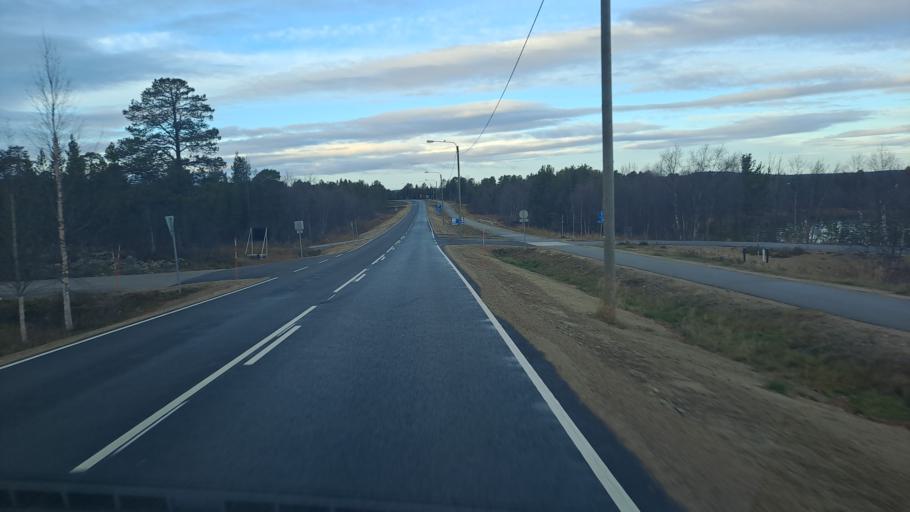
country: FI
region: Lapland
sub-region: Pohjois-Lappi
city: Inari
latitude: 68.9012
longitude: 27.0662
